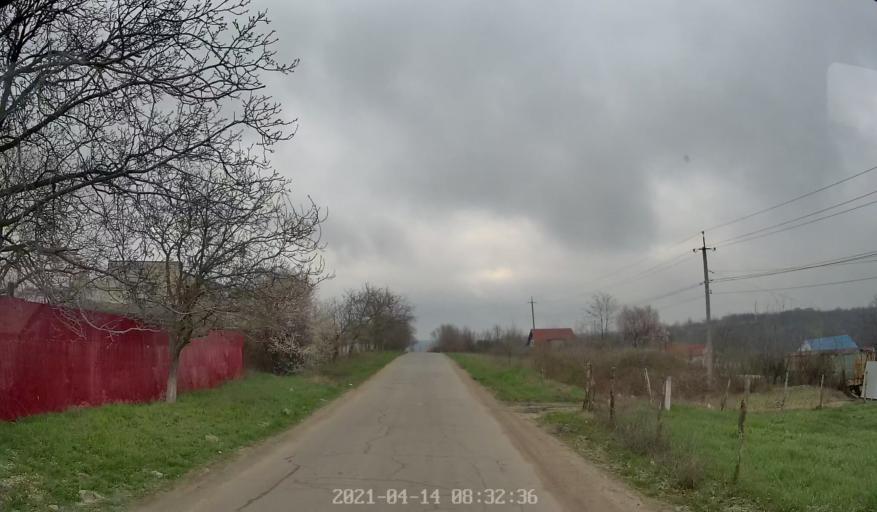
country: MD
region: Chisinau
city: Stauceni
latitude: 47.0589
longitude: 28.9417
